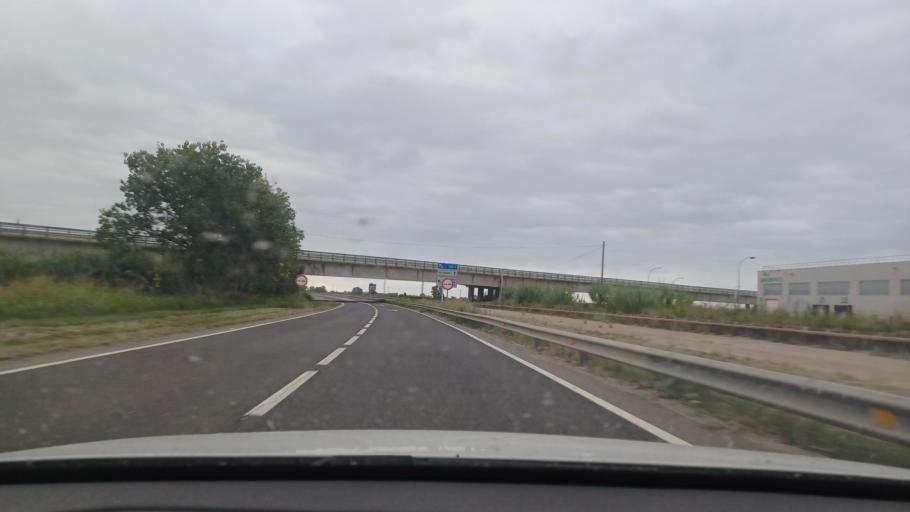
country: ES
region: Catalonia
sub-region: Provincia de Tarragona
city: Amposta
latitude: 40.7149
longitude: 0.5919
